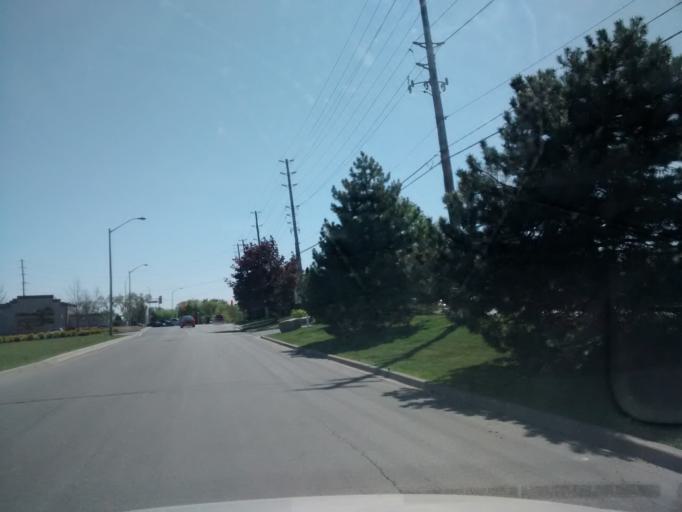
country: CA
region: Ontario
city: Burlington
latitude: 43.3570
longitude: -79.8080
